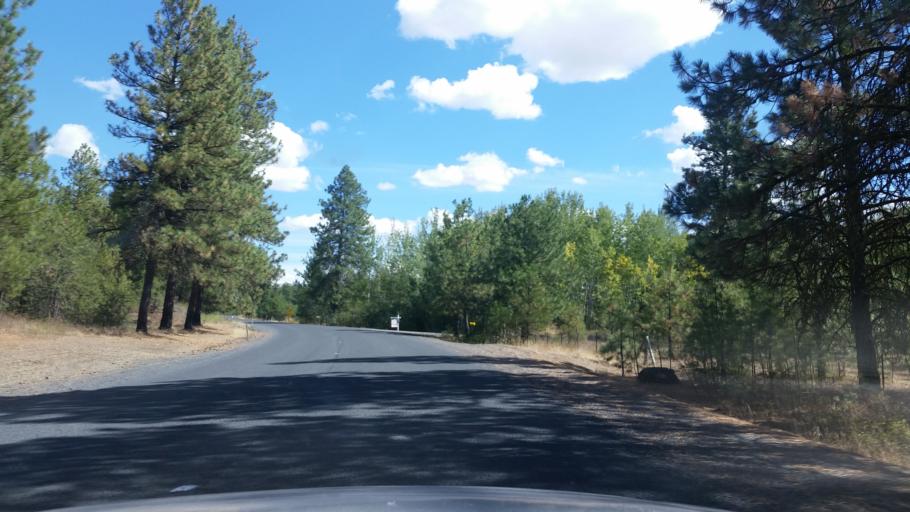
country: US
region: Washington
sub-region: Spokane County
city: Medical Lake
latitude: 47.5008
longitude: -117.6629
